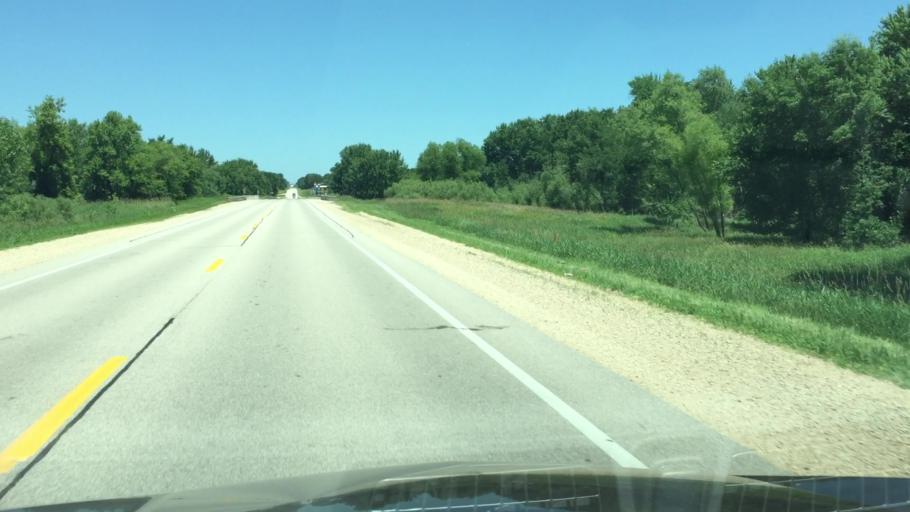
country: US
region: Iowa
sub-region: Cedar County
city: Mechanicsville
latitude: 42.0158
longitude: -91.1367
